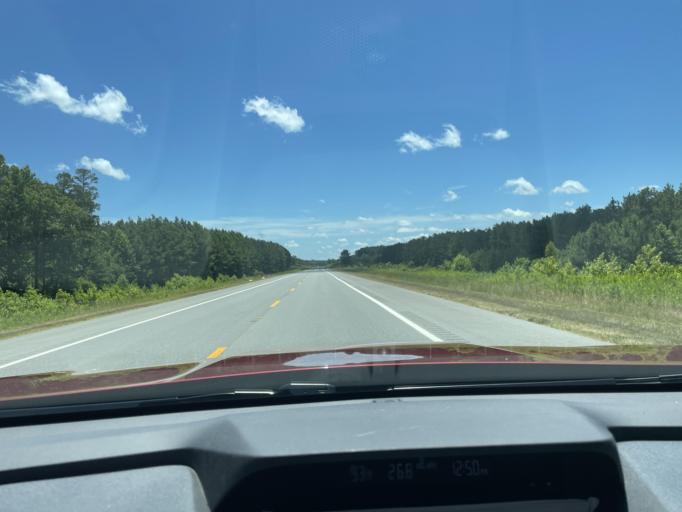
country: US
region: Arkansas
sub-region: Lincoln County
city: Star City
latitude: 33.9528
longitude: -91.9034
